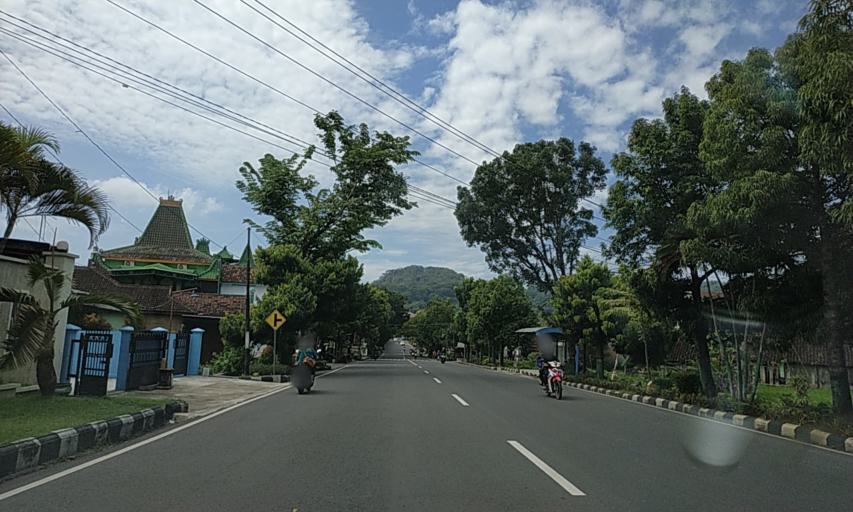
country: ID
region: Central Java
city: Selogiri
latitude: -7.8018
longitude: 110.9115
